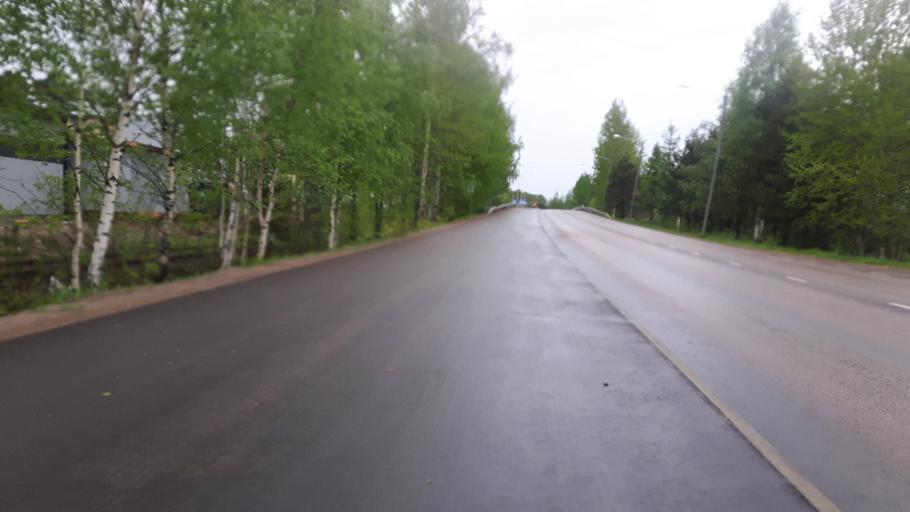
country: FI
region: Kymenlaakso
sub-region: Kotka-Hamina
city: Karhula
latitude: 60.5034
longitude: 26.9019
